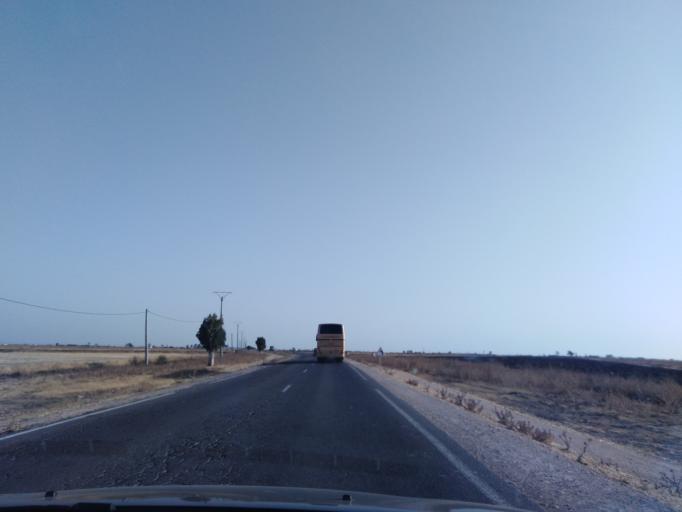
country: MA
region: Doukkala-Abda
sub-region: Safi
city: Youssoufia
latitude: 32.4857
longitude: -8.7672
